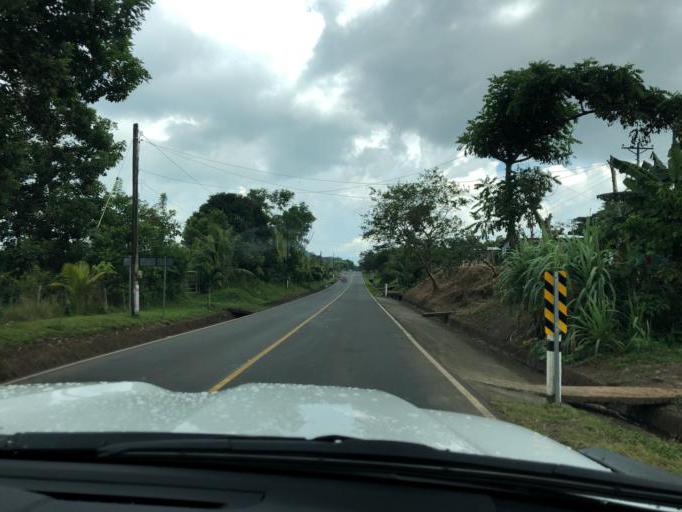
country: NI
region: Chontales
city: Villa Sandino
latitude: 11.9958
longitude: -84.8734
